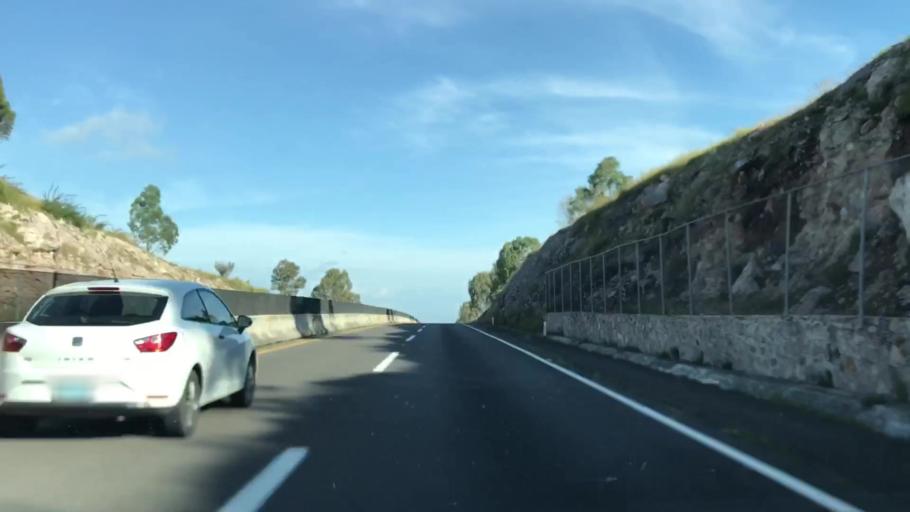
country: MX
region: Jalisco
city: Encarnacion de Diaz
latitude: 21.3846
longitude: -102.1412
